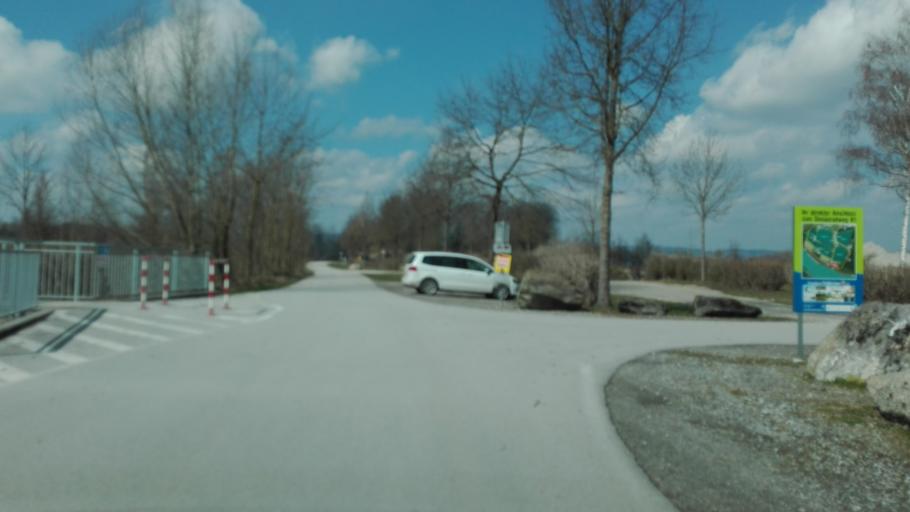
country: AT
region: Upper Austria
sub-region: Politischer Bezirk Urfahr-Umgebung
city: Feldkirchen an der Donau
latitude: 48.3210
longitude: 14.0691
